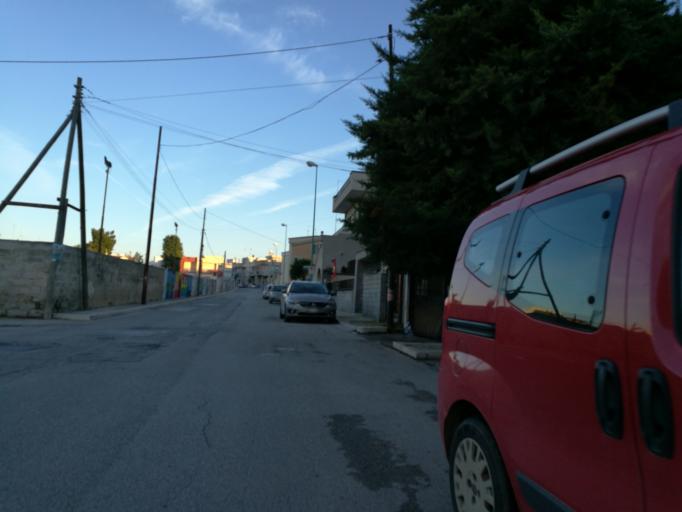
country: IT
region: Apulia
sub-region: Provincia di Bari
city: Adelfia
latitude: 41.0074
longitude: 16.8762
